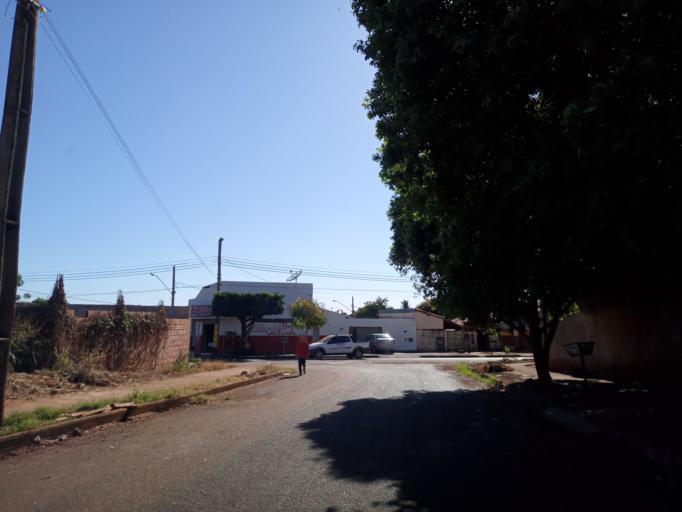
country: BR
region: Minas Gerais
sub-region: Ituiutaba
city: Ituiutaba
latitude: -18.9603
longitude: -49.4547
